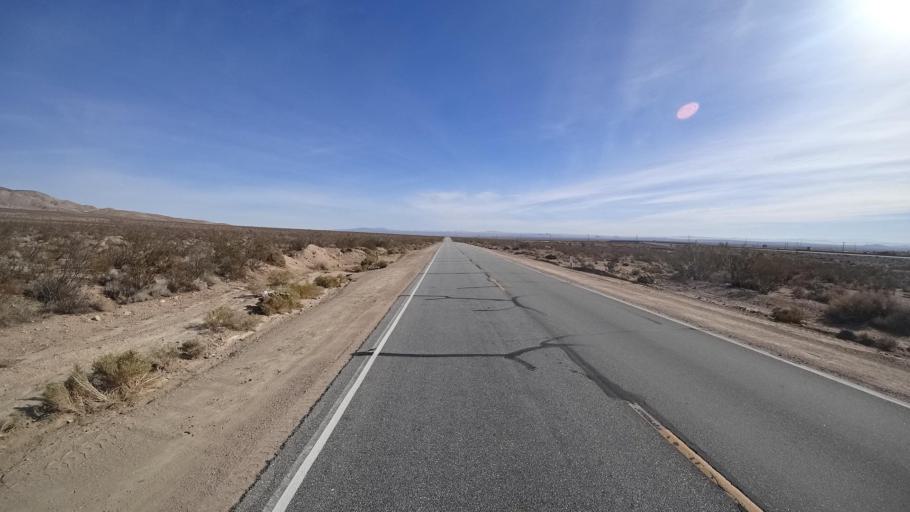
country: US
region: California
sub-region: Kern County
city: Mojave
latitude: 35.1185
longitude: -118.1992
